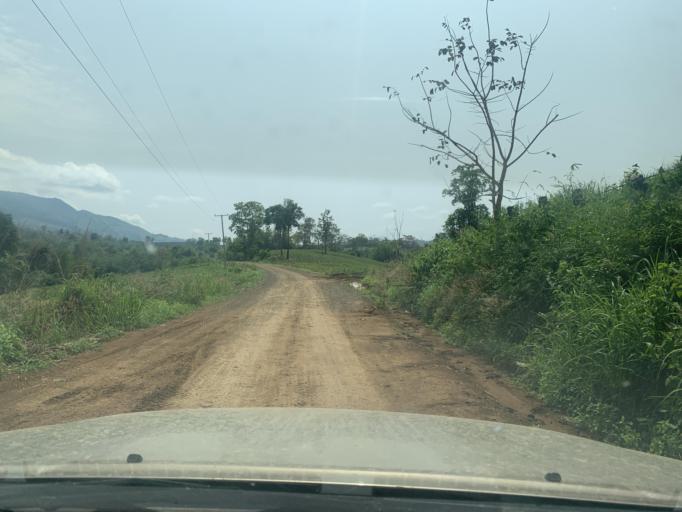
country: TH
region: Uttaradit
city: Ban Khok
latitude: 18.3588
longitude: 101.3837
